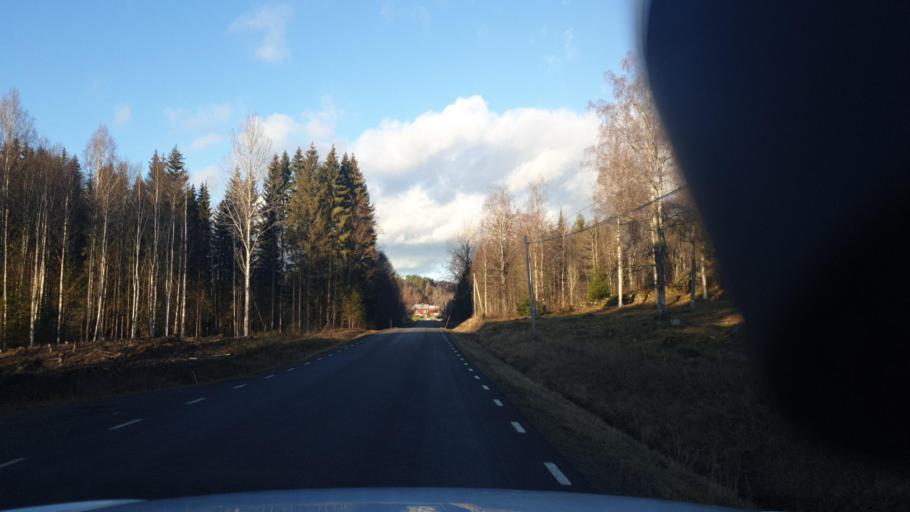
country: SE
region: Vaermland
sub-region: Eda Kommun
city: Charlottenberg
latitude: 59.9265
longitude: 12.5208
